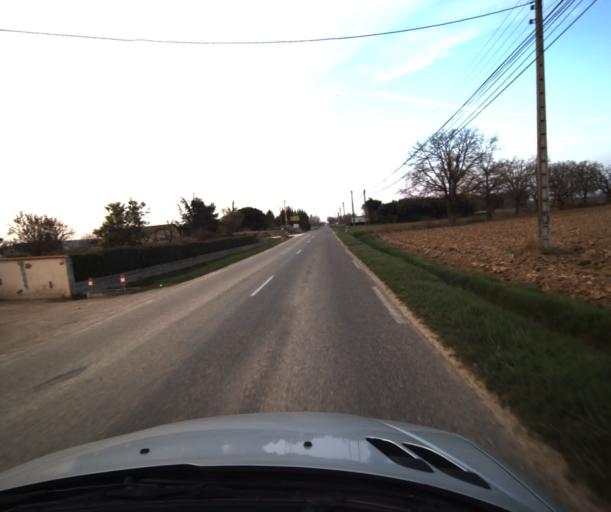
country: FR
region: Midi-Pyrenees
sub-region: Departement de la Haute-Garonne
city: Fronton
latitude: 43.8537
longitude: 1.3857
